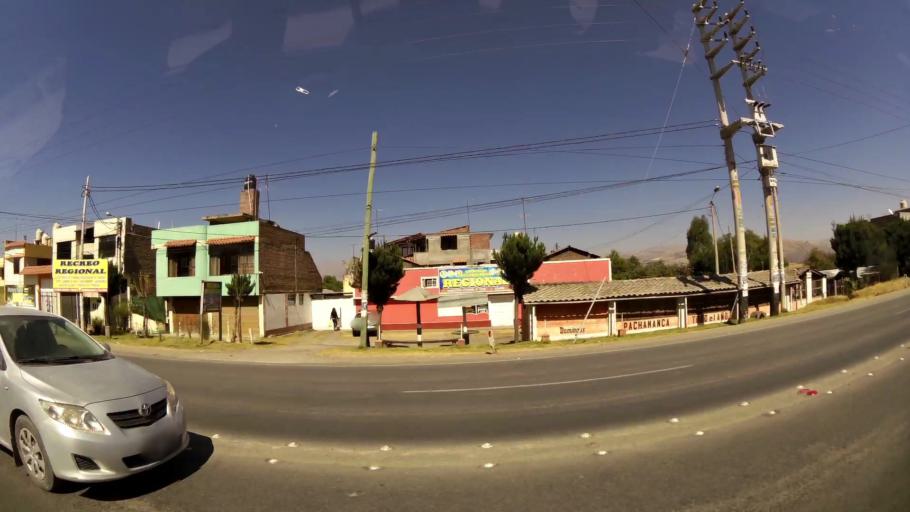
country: PE
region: Junin
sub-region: Provincia de Huancayo
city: San Jeronimo
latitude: -11.9565
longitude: -75.2769
